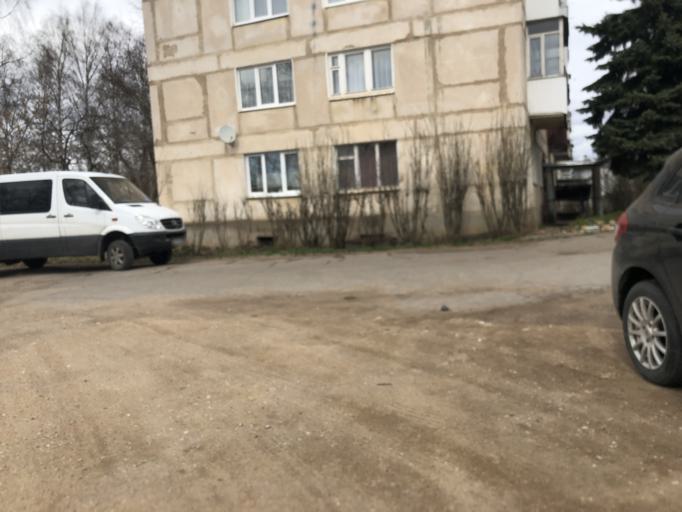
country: RU
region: Tverskaya
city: Rzhev
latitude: 56.2561
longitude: 34.3178
